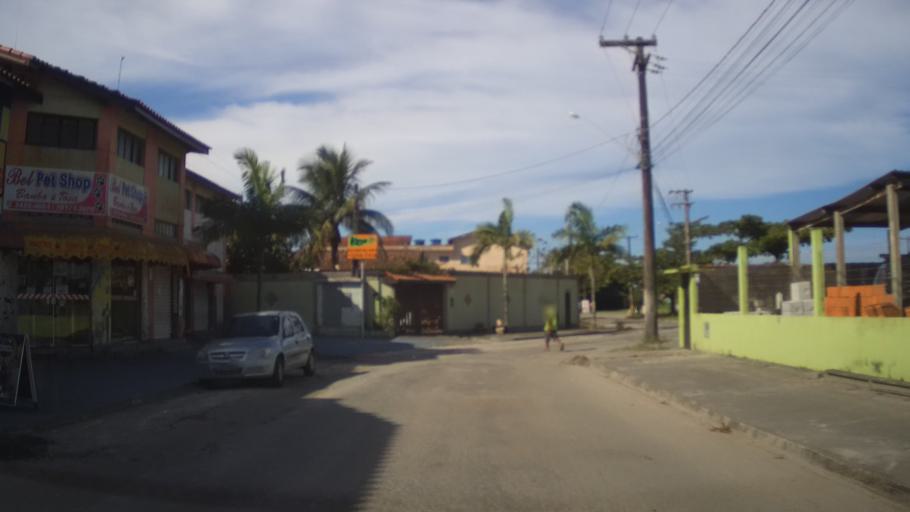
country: BR
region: Sao Paulo
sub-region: Itanhaem
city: Itanhaem
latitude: -24.2058
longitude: -46.8348
